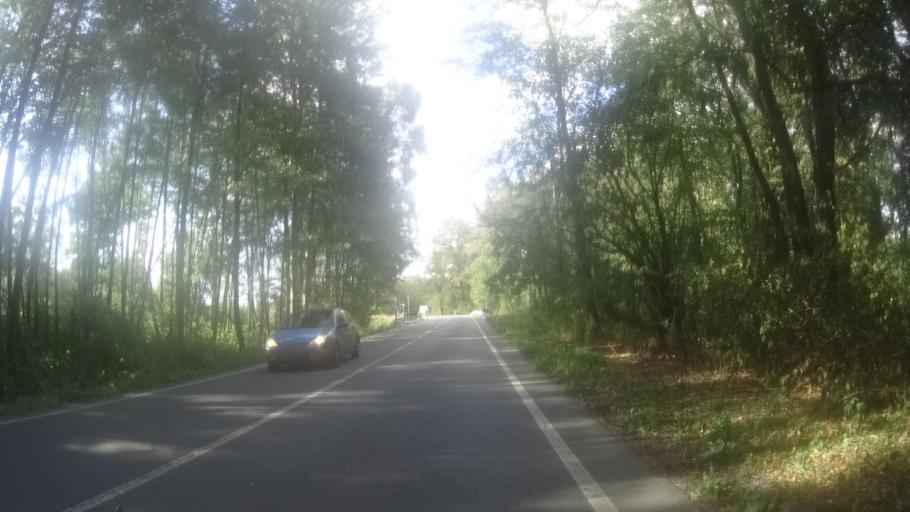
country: CZ
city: Albrechtice nad Orlici
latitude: 50.1288
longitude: 16.0642
